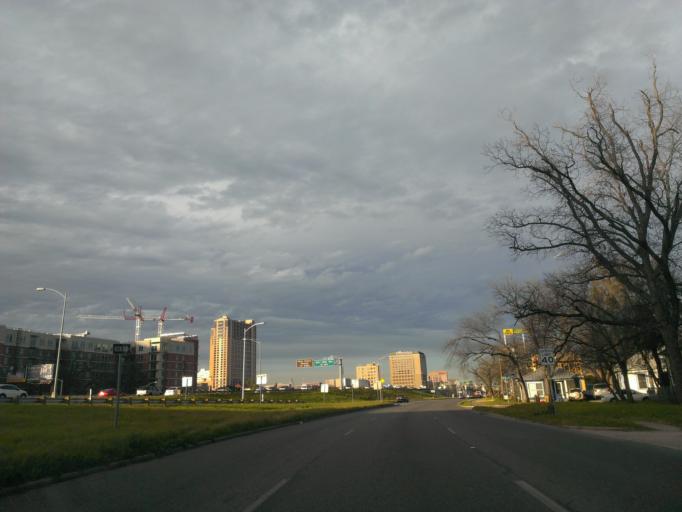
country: US
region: Texas
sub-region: Travis County
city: Austin
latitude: 30.2583
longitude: -97.7366
